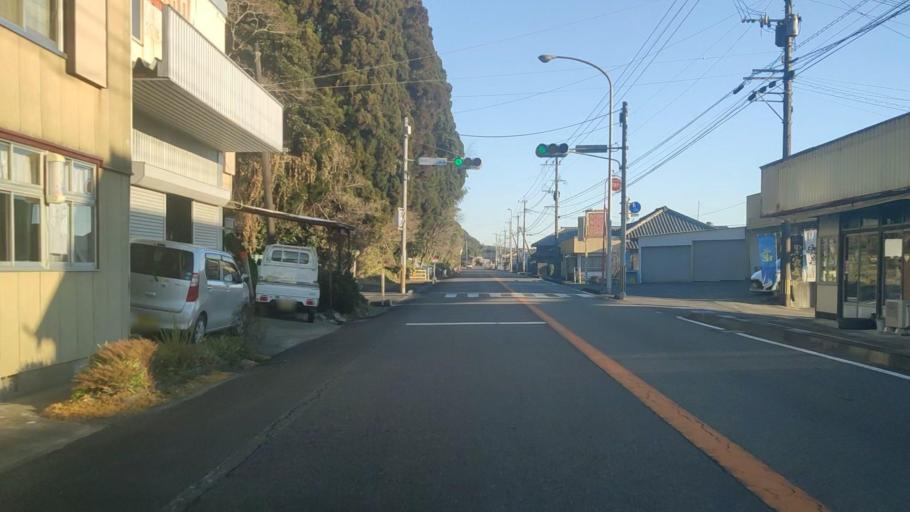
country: JP
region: Miyazaki
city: Takanabe
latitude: 32.0817
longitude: 131.5096
